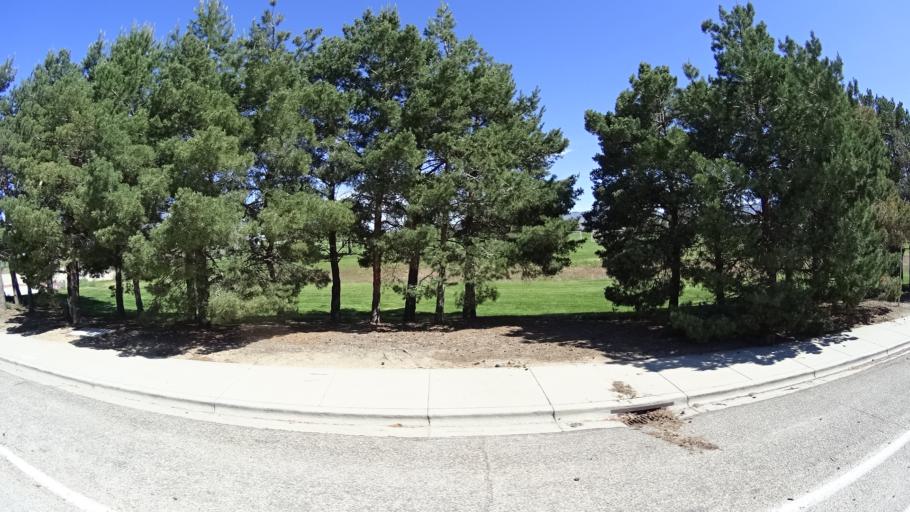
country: US
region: Idaho
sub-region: Ada County
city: Boise
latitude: 43.5444
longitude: -116.1462
